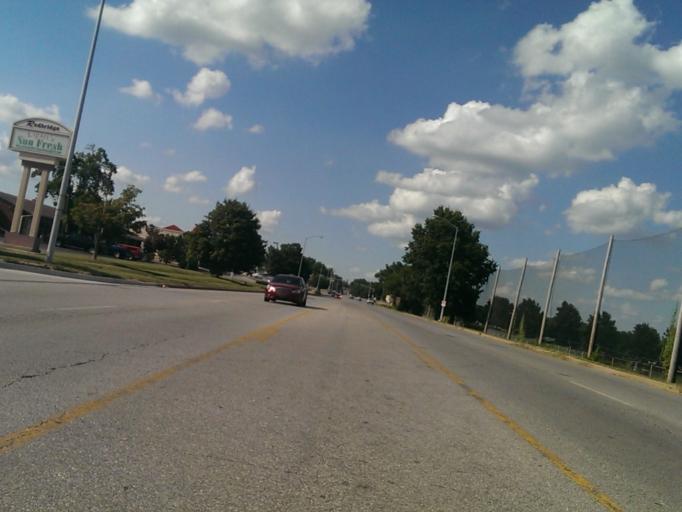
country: US
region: Kansas
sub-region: Johnson County
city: Leawood
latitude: 38.9230
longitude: -94.5836
